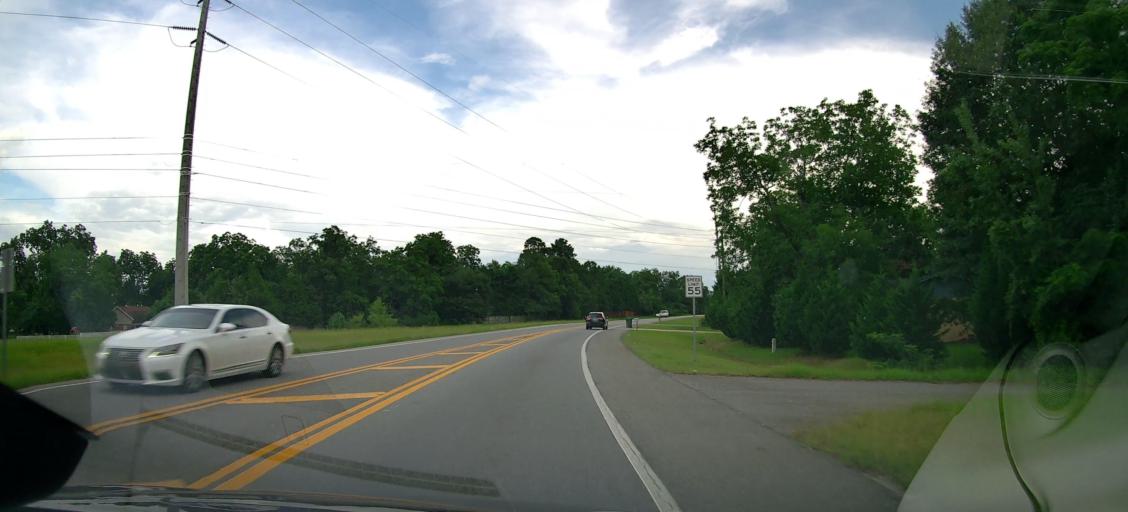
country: US
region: Georgia
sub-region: Houston County
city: Centerville
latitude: 32.6737
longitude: -83.7087
